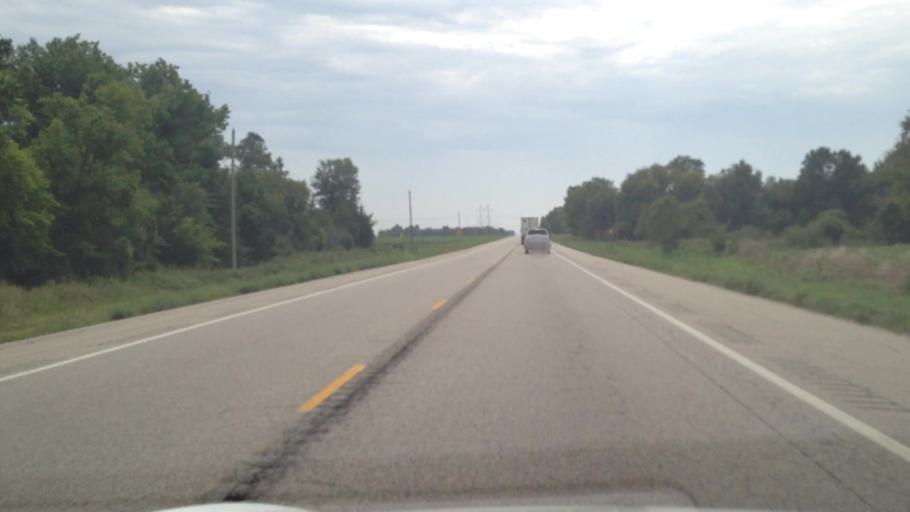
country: US
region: Kansas
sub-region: Crawford County
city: Pittsburg
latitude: 37.2969
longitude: -94.7055
